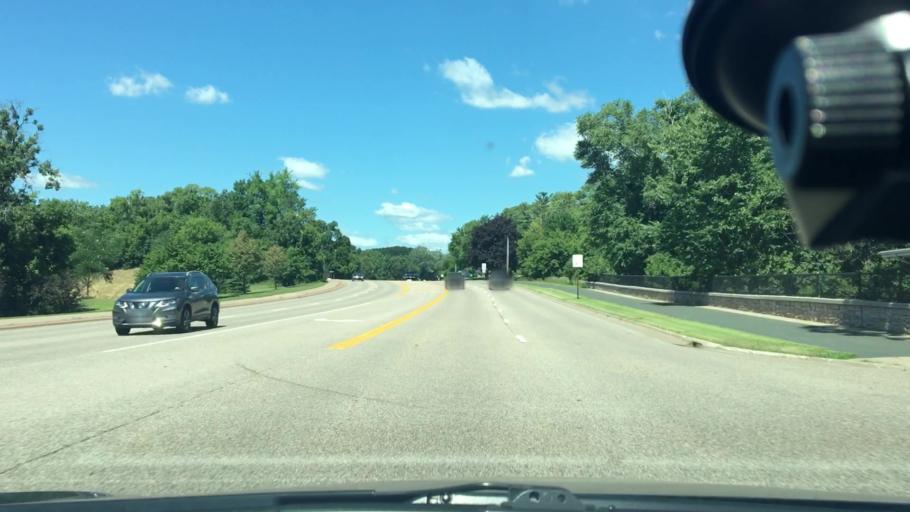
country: US
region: Minnesota
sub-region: Hennepin County
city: Maple Grove
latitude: 45.0725
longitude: -93.4556
